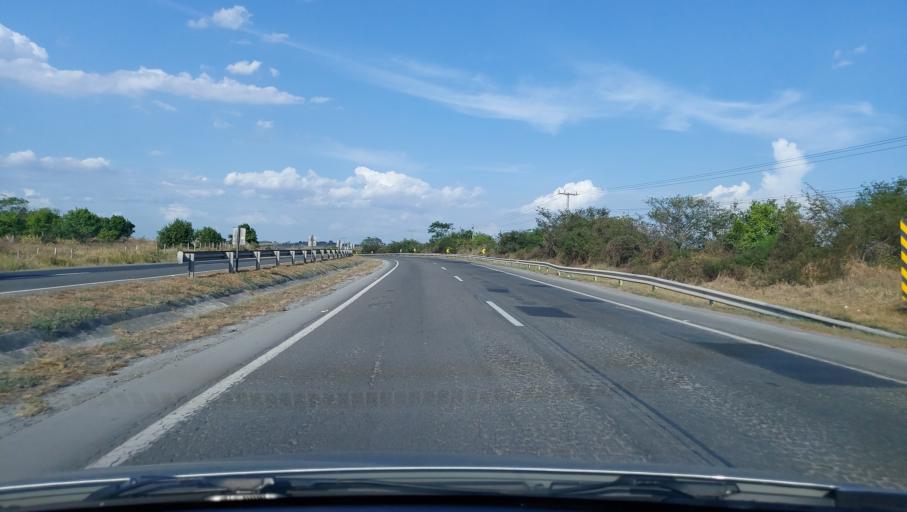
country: BR
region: Bahia
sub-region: Feira De Santana
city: Feira de Santana
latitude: -12.3193
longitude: -39.0464
